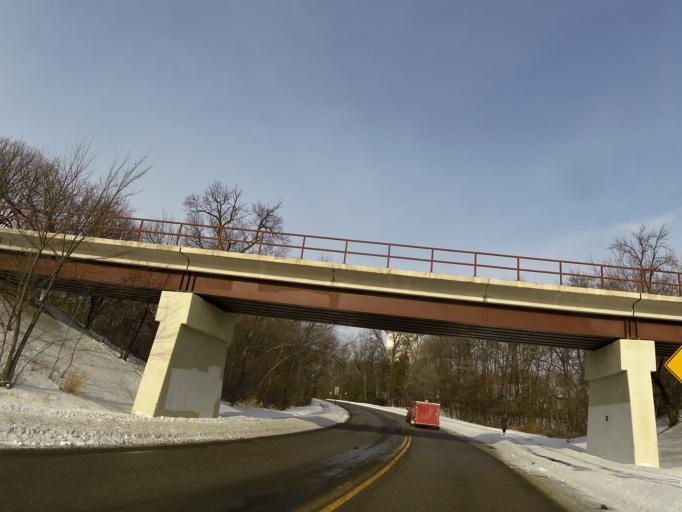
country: US
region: Minnesota
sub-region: Carver County
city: Chanhassen
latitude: 44.8674
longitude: -93.5113
